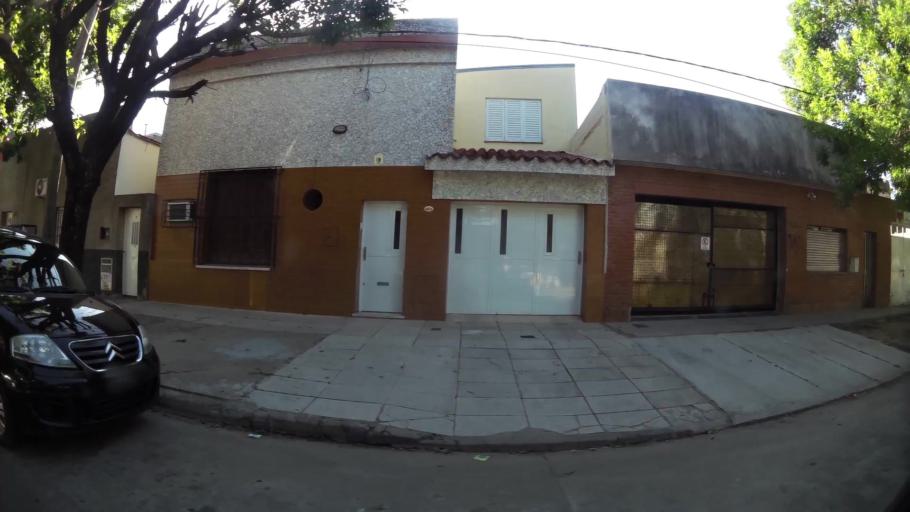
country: AR
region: Santa Fe
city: Santa Fe de la Vera Cruz
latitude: -31.6097
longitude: -60.6957
